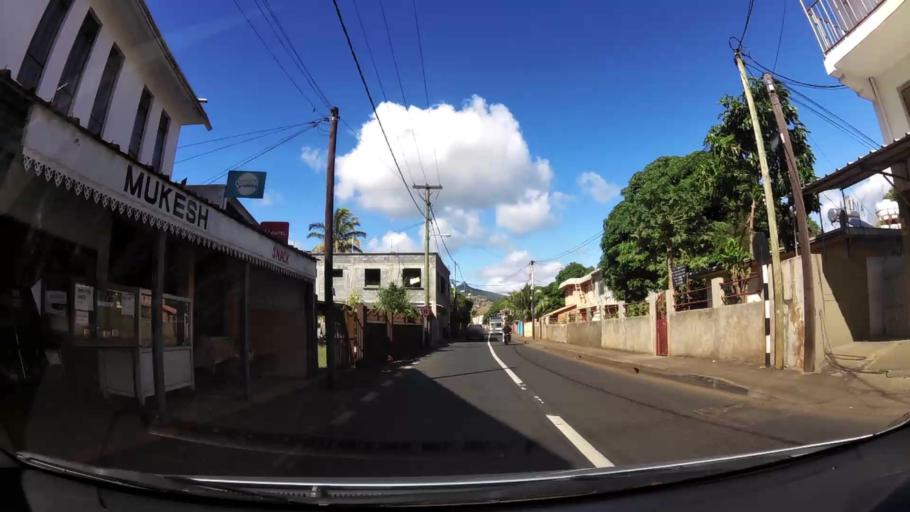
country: MU
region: Pamplemousses
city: Le Hochet
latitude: -20.1328
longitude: 57.5224
